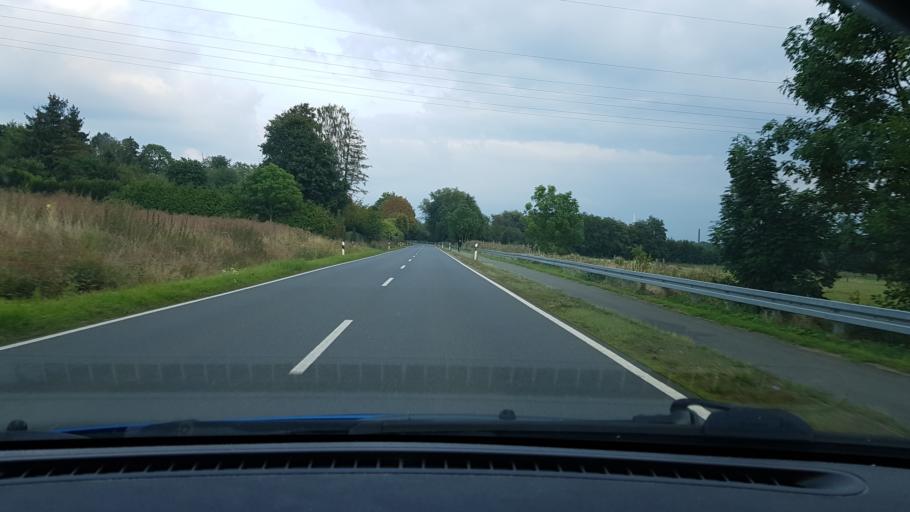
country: DE
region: Lower Saxony
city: Bad Munder am Deister
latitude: 52.1992
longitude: 9.4319
